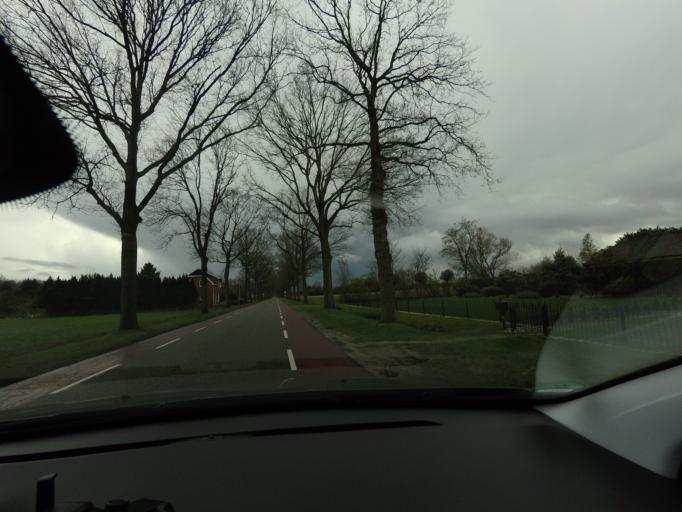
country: NL
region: Drenthe
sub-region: Gemeente Borger-Odoorn
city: Borger
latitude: 52.9840
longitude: 6.7831
